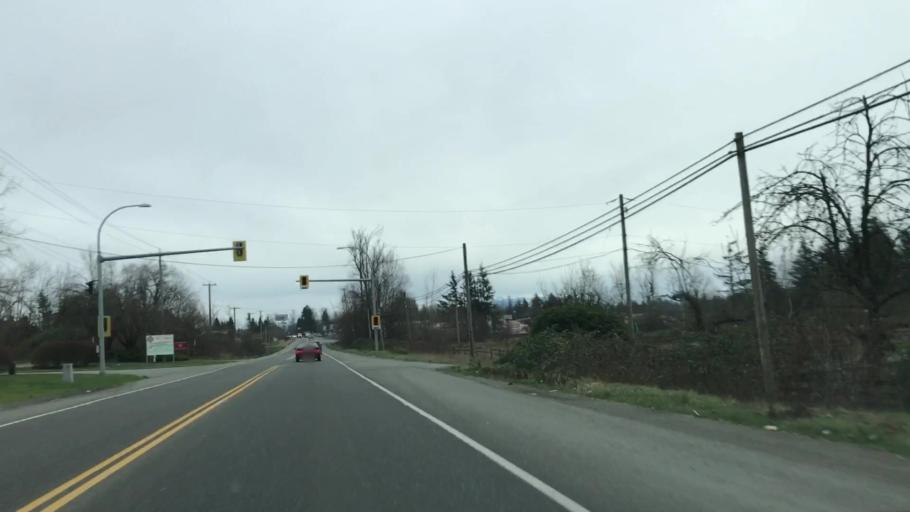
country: CA
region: British Columbia
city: Aldergrove
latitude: 49.0571
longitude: -122.4370
